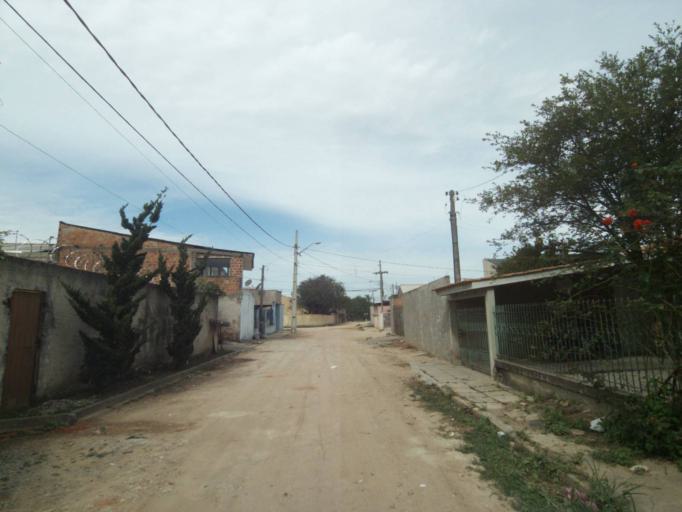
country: BR
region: Parana
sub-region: Pinhais
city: Pinhais
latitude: -25.4294
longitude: -49.2057
